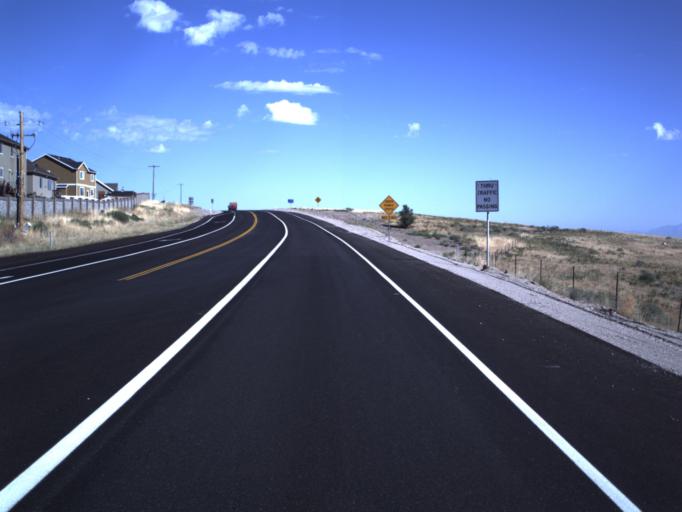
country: US
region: Utah
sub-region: Salt Lake County
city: Oquirrh
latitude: 40.6313
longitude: -112.0533
